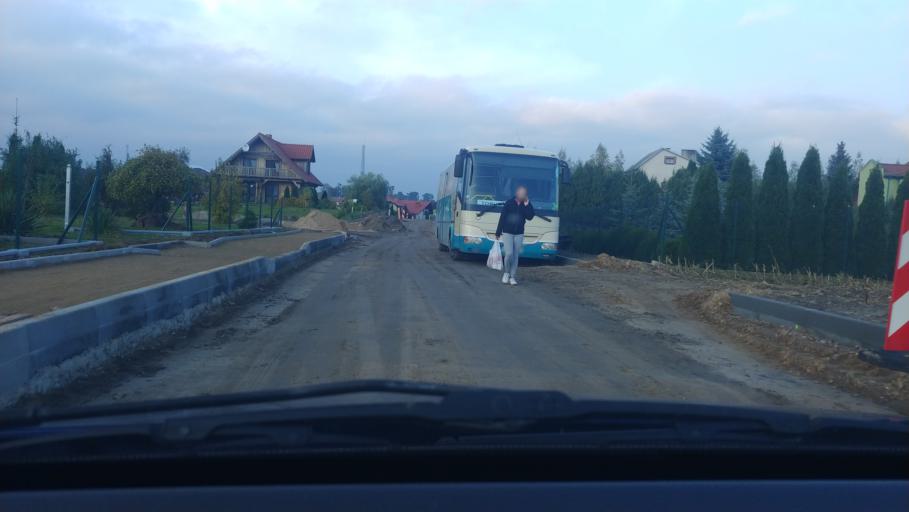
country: PL
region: Kujawsko-Pomorskie
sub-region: Powiat brodnicki
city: Gorzno
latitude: 53.1919
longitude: 19.6374
